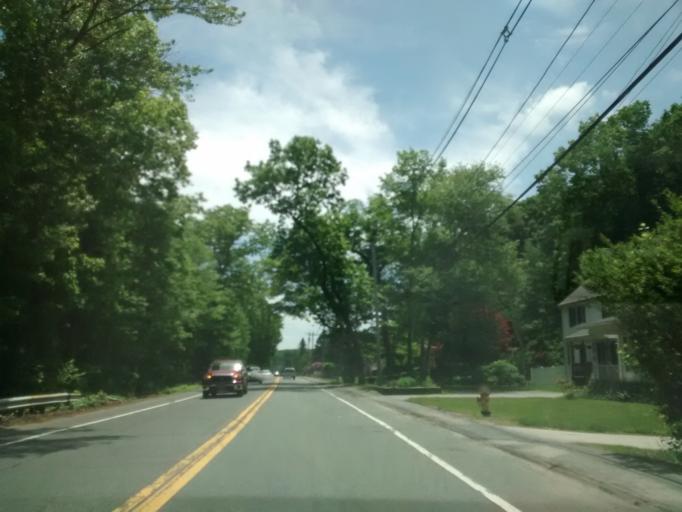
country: US
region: Massachusetts
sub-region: Worcester County
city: Northbridge
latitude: 42.1332
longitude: -71.6481
